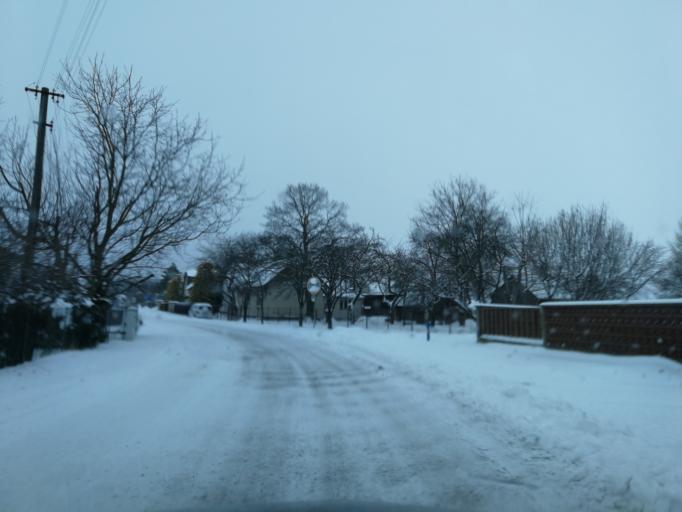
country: CZ
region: Vysocina
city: Heralec
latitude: 49.5288
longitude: 15.4640
